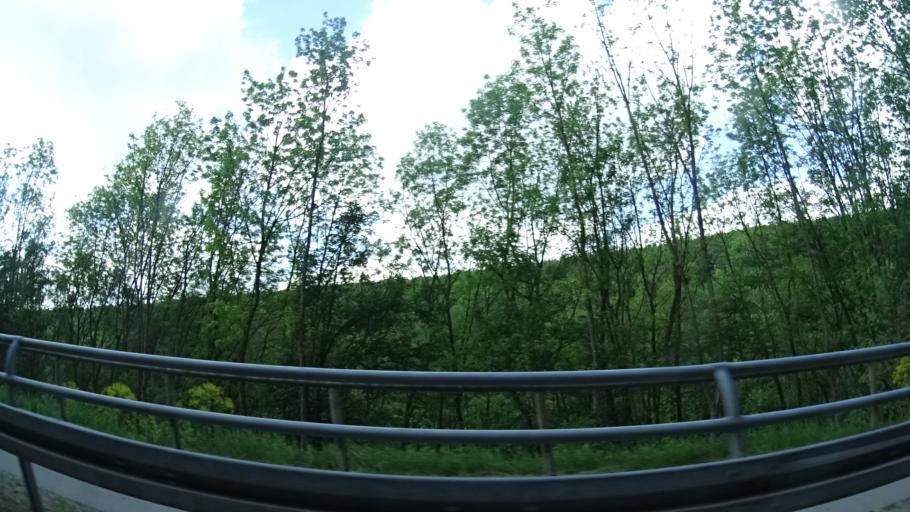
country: DE
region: Bavaria
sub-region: Regierungsbezirk Unterfranken
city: Sandberg
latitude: 50.3374
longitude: 9.9917
